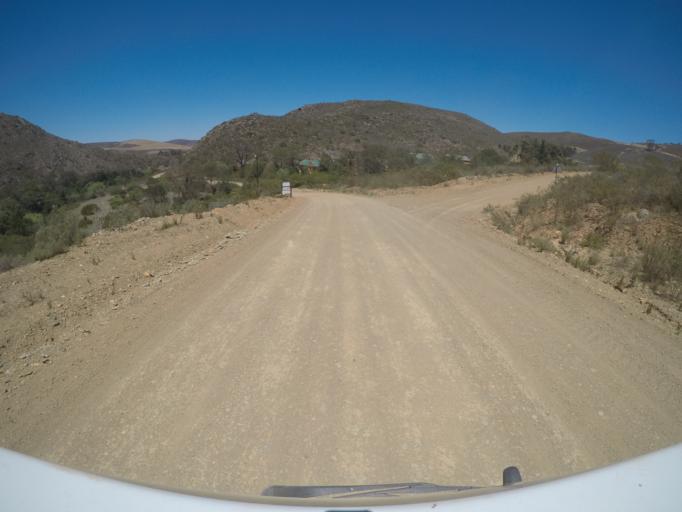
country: ZA
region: Western Cape
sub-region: Overberg District Municipality
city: Grabouw
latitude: -34.1164
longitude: 19.2339
